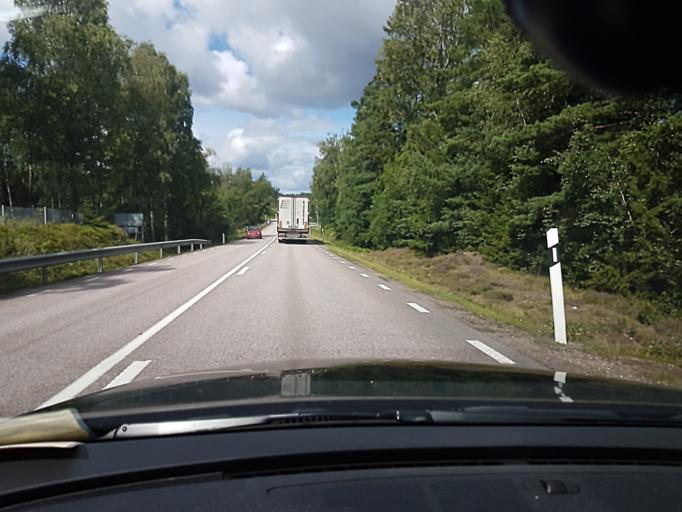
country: SE
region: Kronoberg
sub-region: Lessebo Kommun
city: Hovmantorp
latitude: 56.7896
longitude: 15.1400
